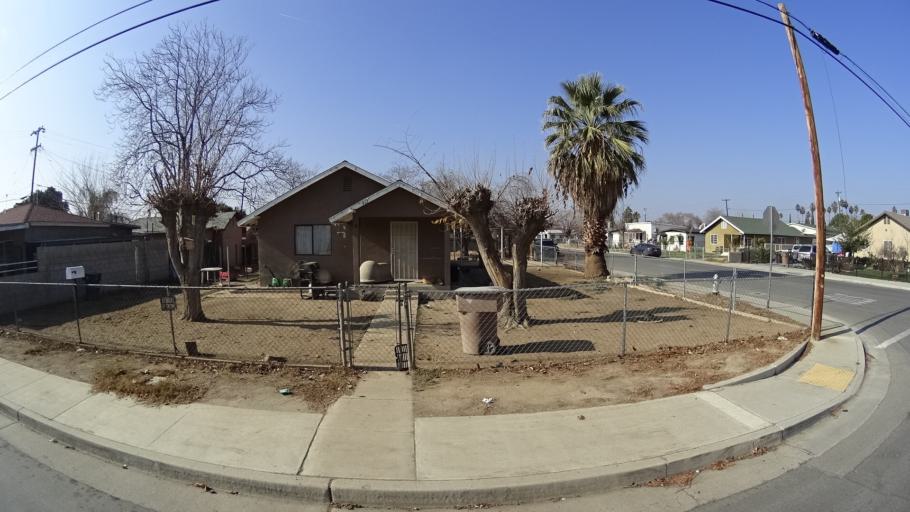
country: US
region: California
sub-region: Kern County
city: Bakersfield
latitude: 35.3664
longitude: -118.9959
